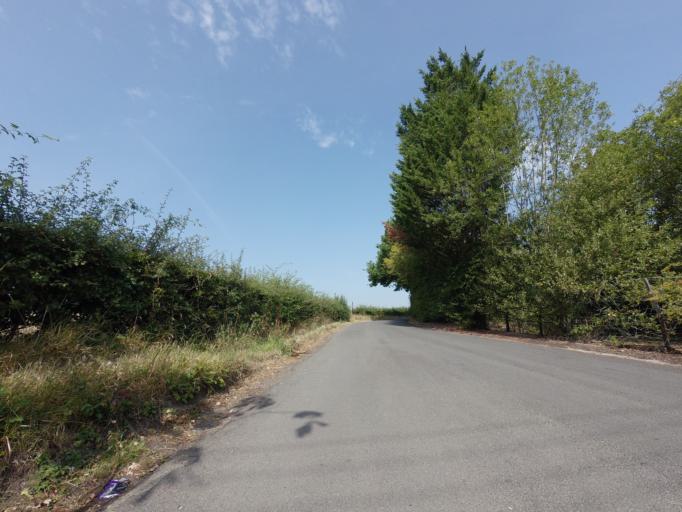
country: GB
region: England
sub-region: Kent
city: Staplehurst
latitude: 51.1257
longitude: 0.5839
